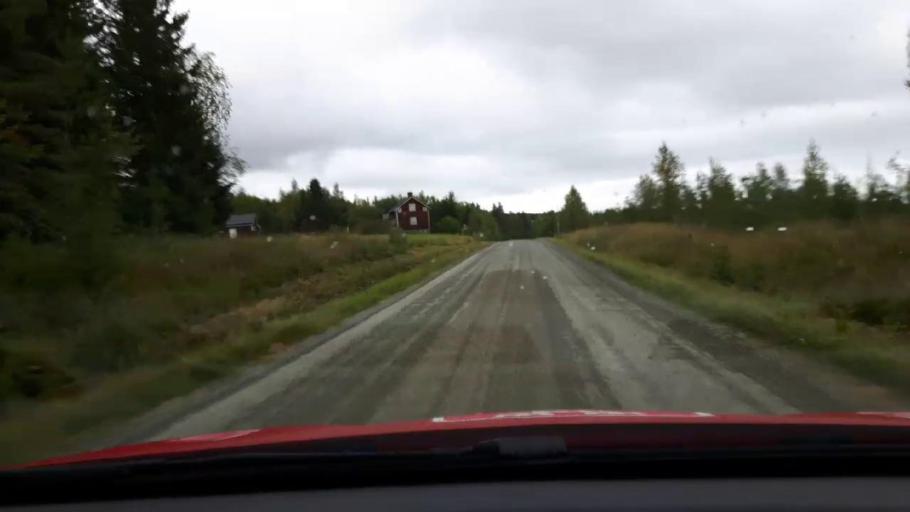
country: SE
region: Jaemtland
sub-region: Bergs Kommun
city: Hoverberg
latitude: 62.8704
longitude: 14.3002
